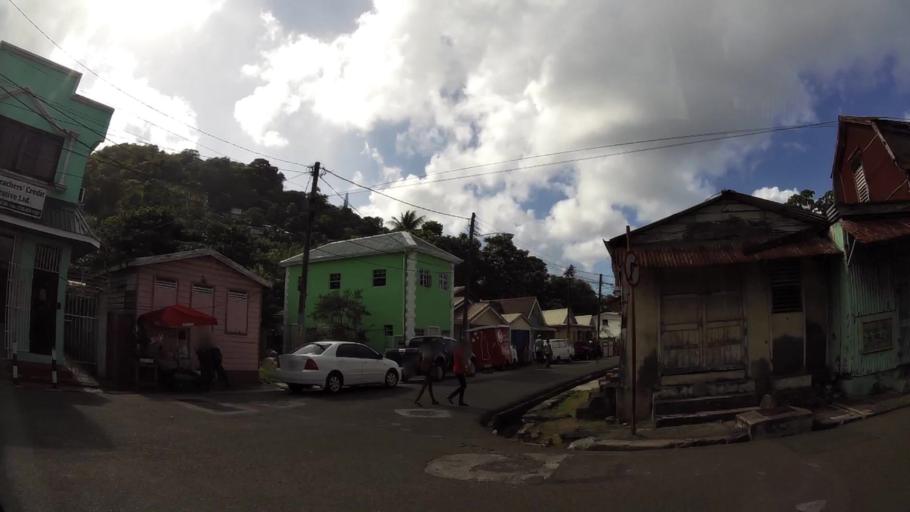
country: LC
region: Castries Quarter
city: Castries
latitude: 14.0067
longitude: -60.9882
